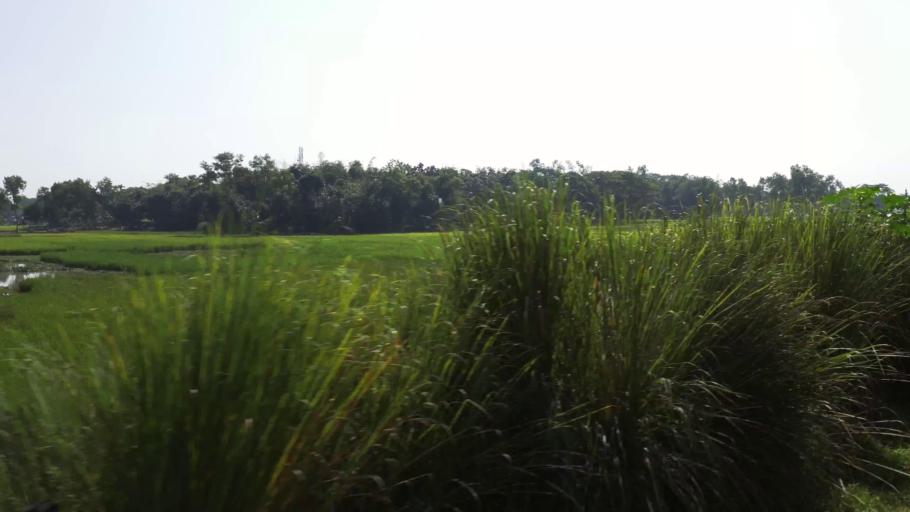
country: BD
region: Dhaka
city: Gafargaon
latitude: 24.5691
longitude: 90.5082
